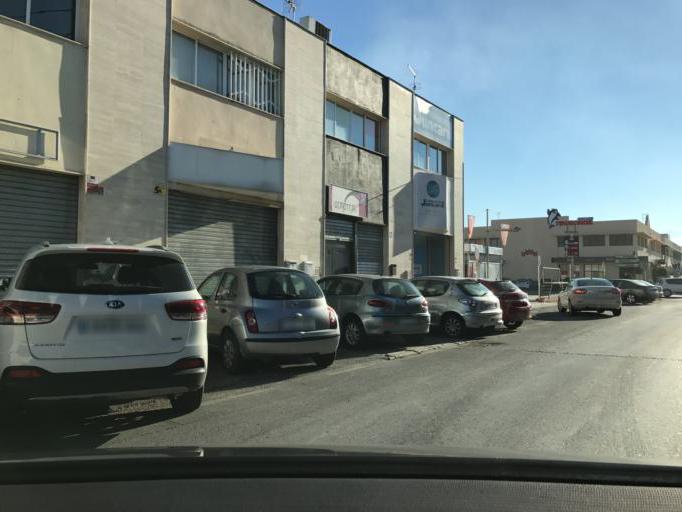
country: ES
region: Andalusia
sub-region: Provincia de Granada
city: Albolote
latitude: 37.2302
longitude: -3.6464
